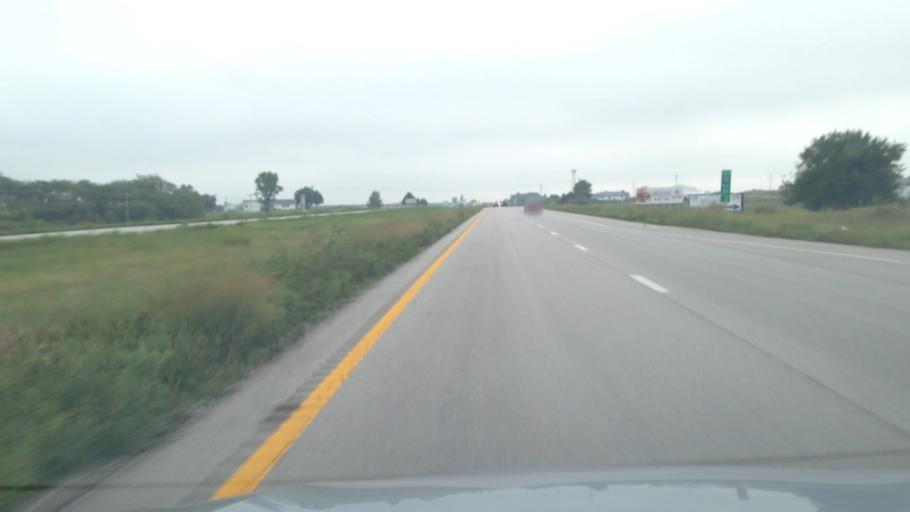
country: US
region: Missouri
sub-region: Clinton County
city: Cameron
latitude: 39.8502
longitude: -94.1784
